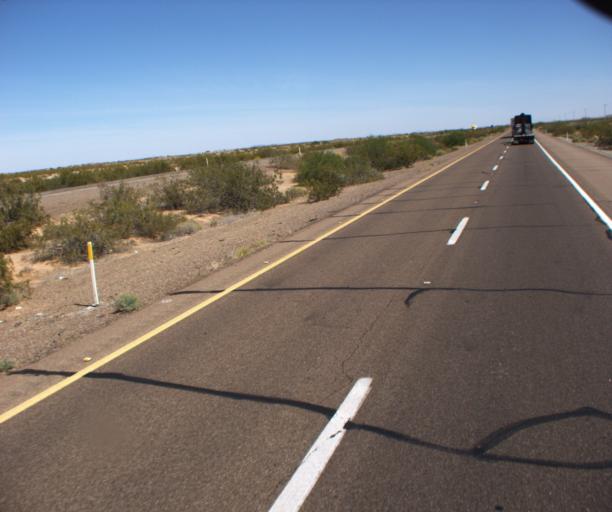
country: US
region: Arizona
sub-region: Yuma County
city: Wellton
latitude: 32.7742
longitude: -113.5998
